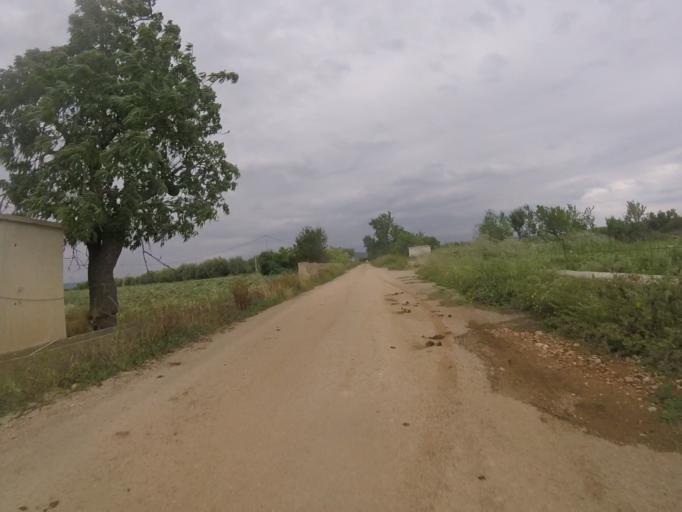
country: ES
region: Valencia
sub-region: Provincia de Castello
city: Torreblanca
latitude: 40.2170
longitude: 0.2281
